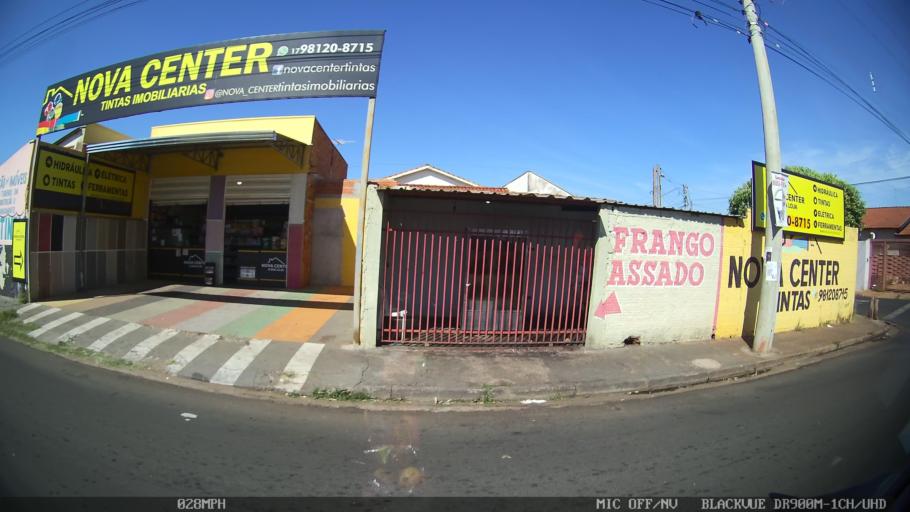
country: BR
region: Sao Paulo
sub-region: Sao Jose Do Rio Preto
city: Sao Jose do Rio Preto
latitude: -20.7665
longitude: -49.3998
